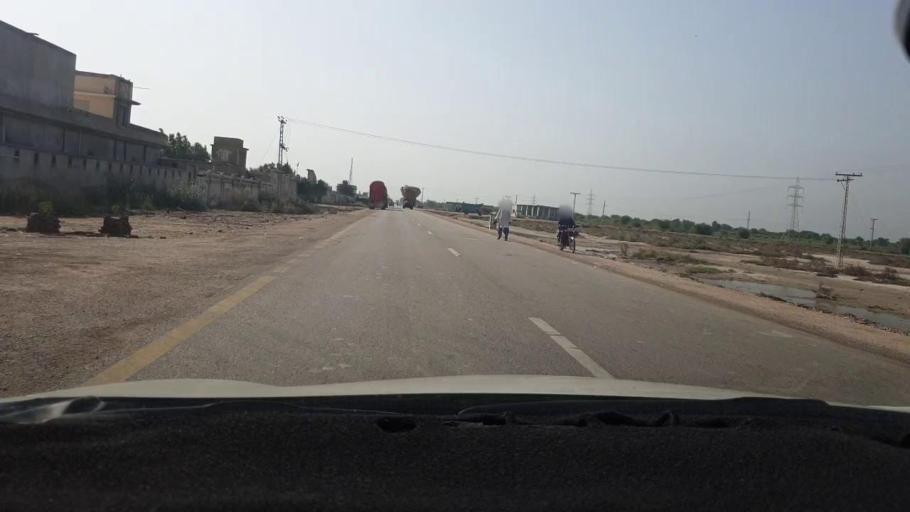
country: PK
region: Sindh
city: Sanghar
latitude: 25.9703
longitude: 68.9715
